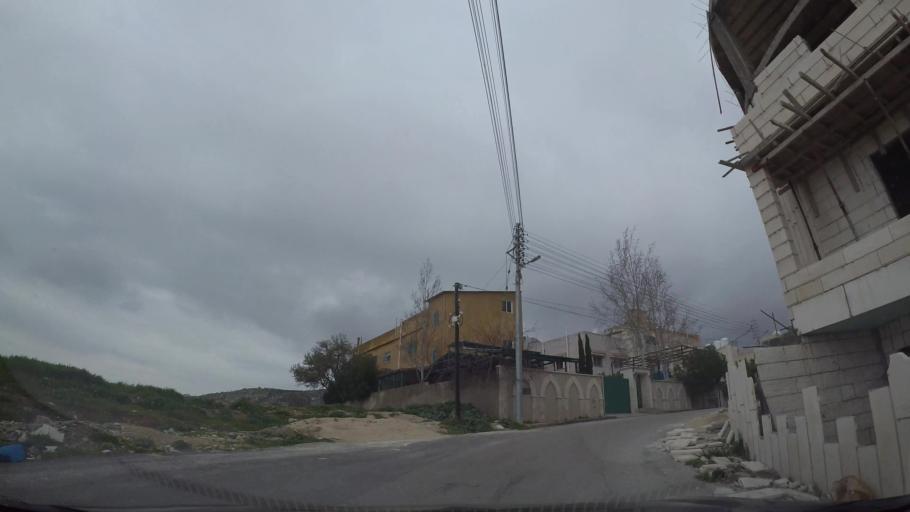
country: JO
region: Amman
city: Wadi as Sir
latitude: 31.9455
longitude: 35.8149
